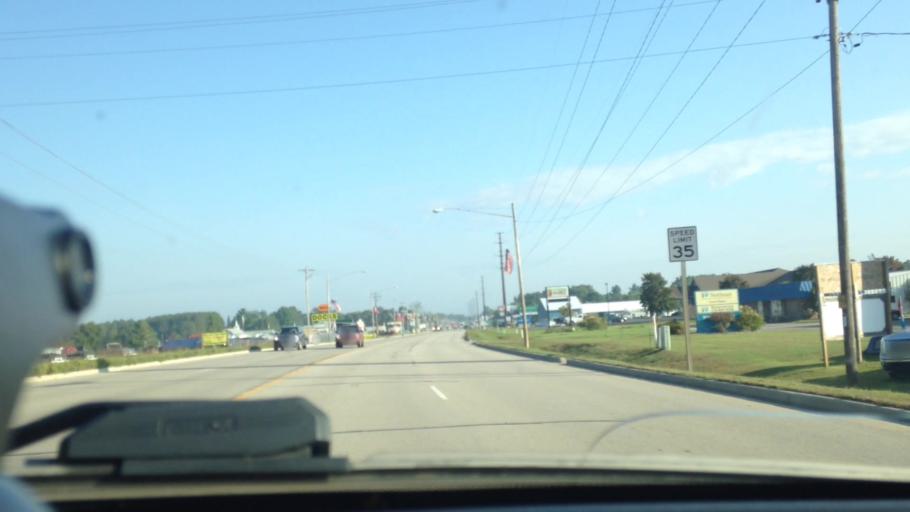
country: US
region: Wisconsin
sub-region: Marinette County
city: Peshtigo
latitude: 45.2196
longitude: -87.9971
